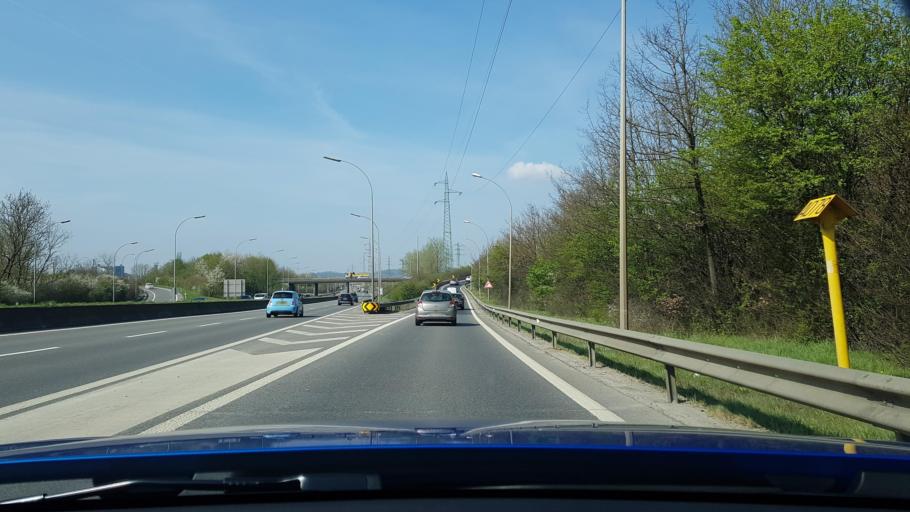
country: LU
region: Luxembourg
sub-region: Canton d'Esch-sur-Alzette
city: Esch-sur-Alzette
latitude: 49.5137
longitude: 5.9792
